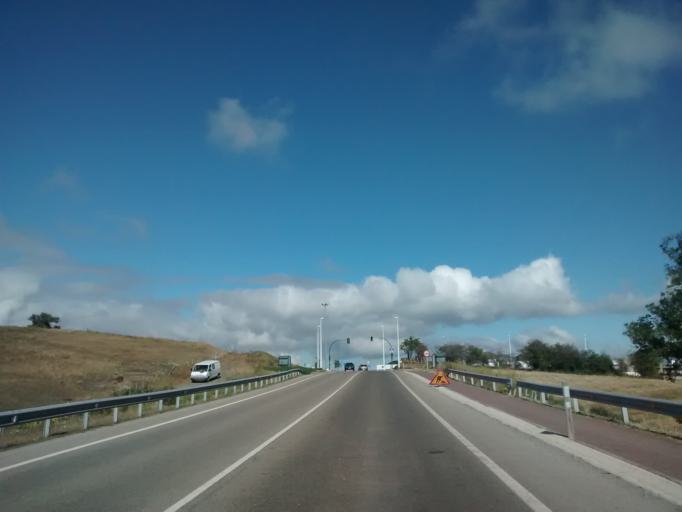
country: ES
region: Cantabria
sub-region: Provincia de Cantabria
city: Reinosa
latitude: 43.0070
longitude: -4.1351
